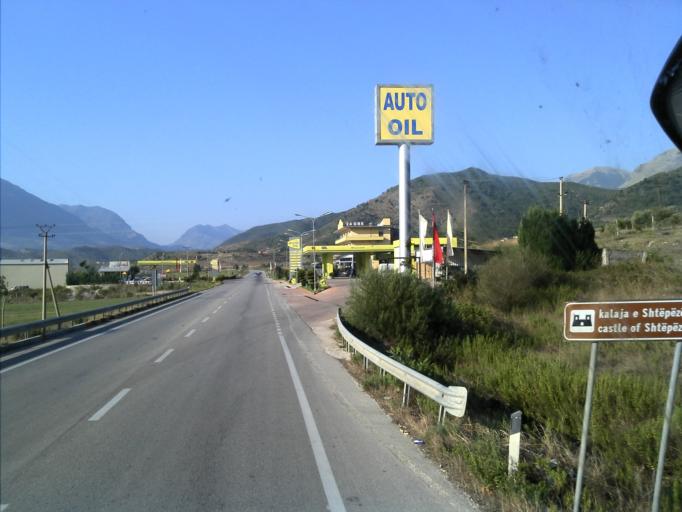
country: AL
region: Gjirokaster
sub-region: Rrethi i Gjirokastres
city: Picar
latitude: 40.1890
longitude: 20.0805
